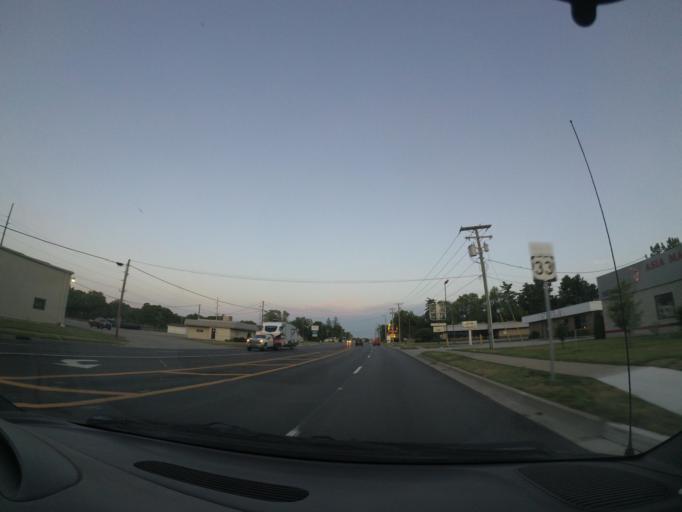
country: US
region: Indiana
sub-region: Elkhart County
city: Dunlap
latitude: 41.6493
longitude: -85.9387
